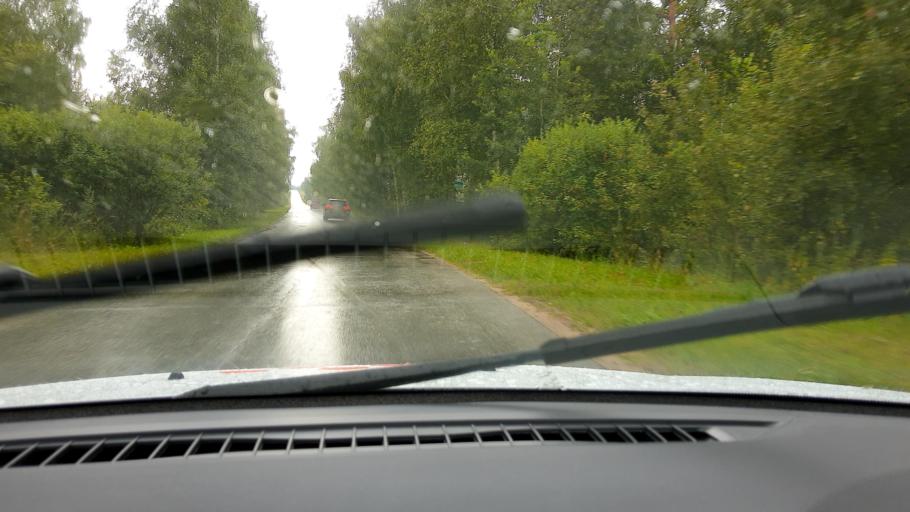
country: RU
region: Nizjnij Novgorod
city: Surovatikha
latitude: 55.9532
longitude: 43.9531
